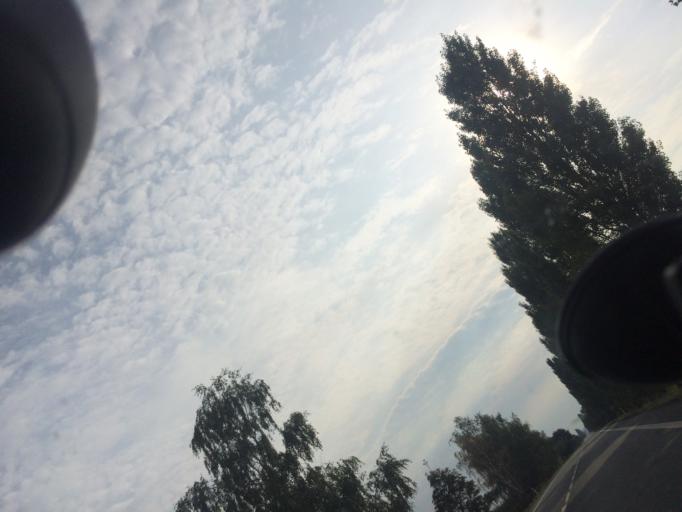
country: CZ
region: Central Bohemia
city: Poricany
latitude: 50.0509
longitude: 14.9380
